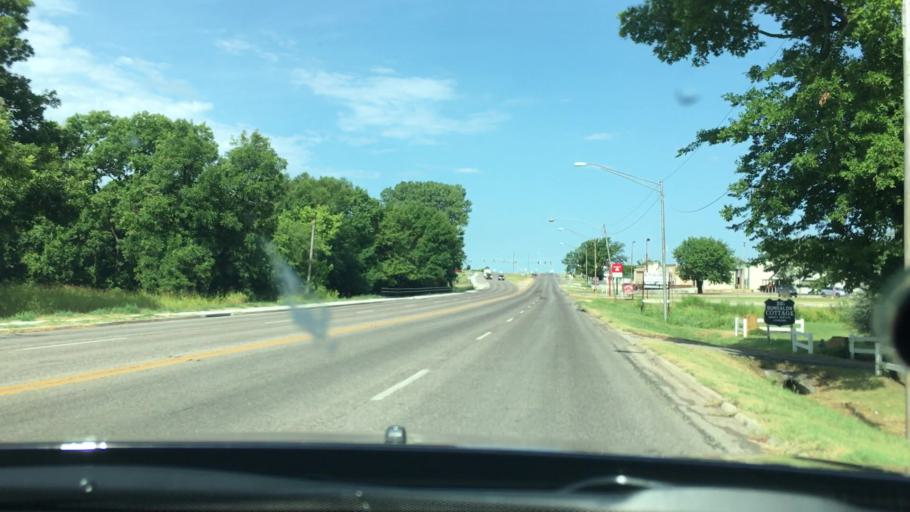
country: US
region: Oklahoma
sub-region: Murray County
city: Sulphur
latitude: 34.5064
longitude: -96.9978
